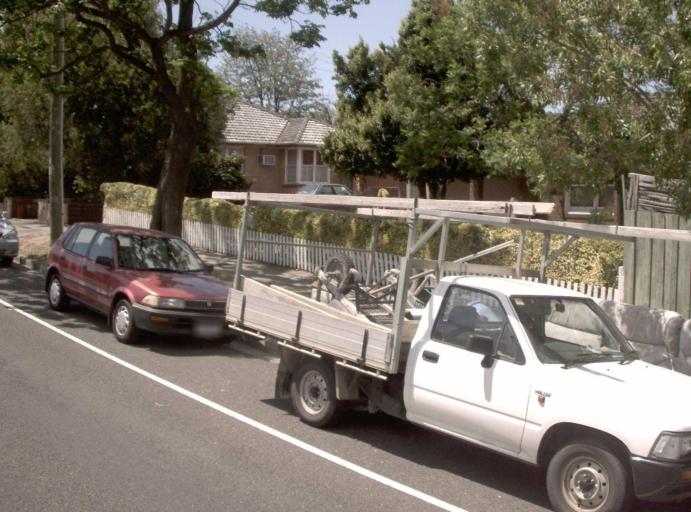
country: AU
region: Victoria
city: Highett
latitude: -37.9343
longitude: 145.0618
